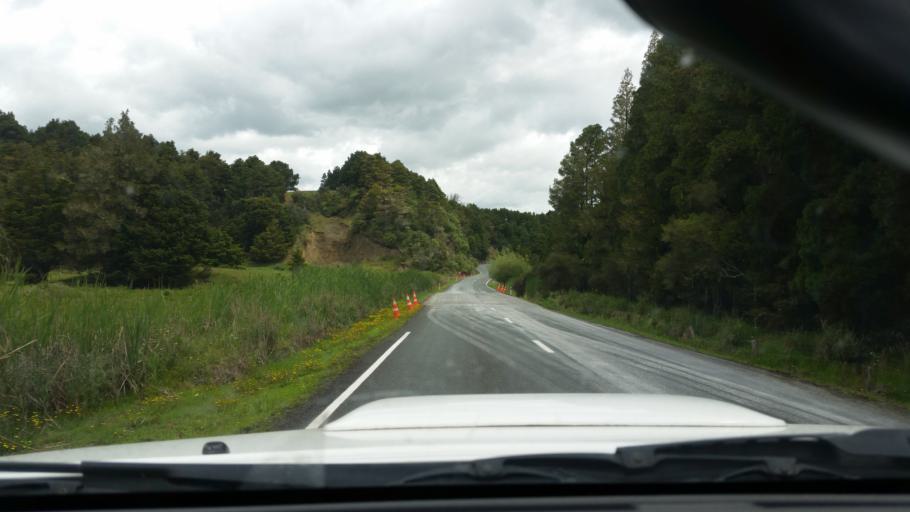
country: NZ
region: Northland
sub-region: Kaipara District
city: Dargaville
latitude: -35.7759
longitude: 173.9071
